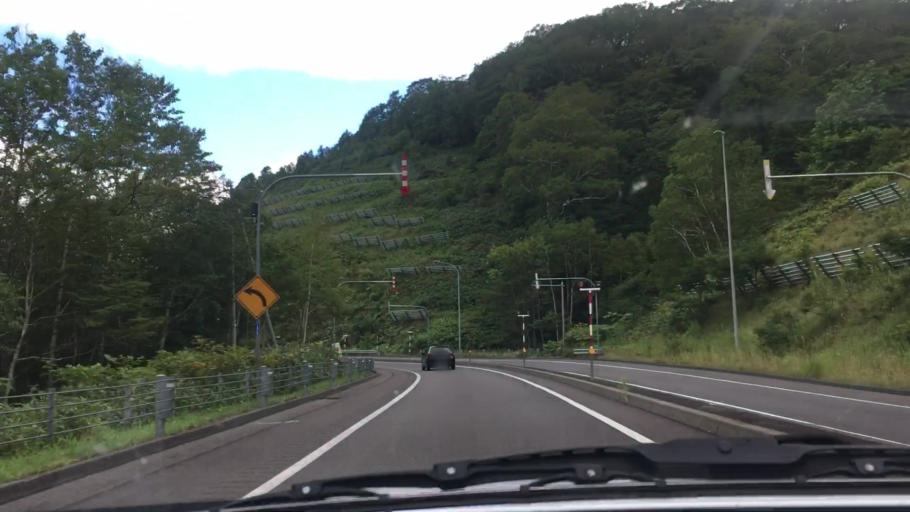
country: JP
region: Hokkaido
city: Shimo-furano
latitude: 43.1503
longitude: 142.7735
